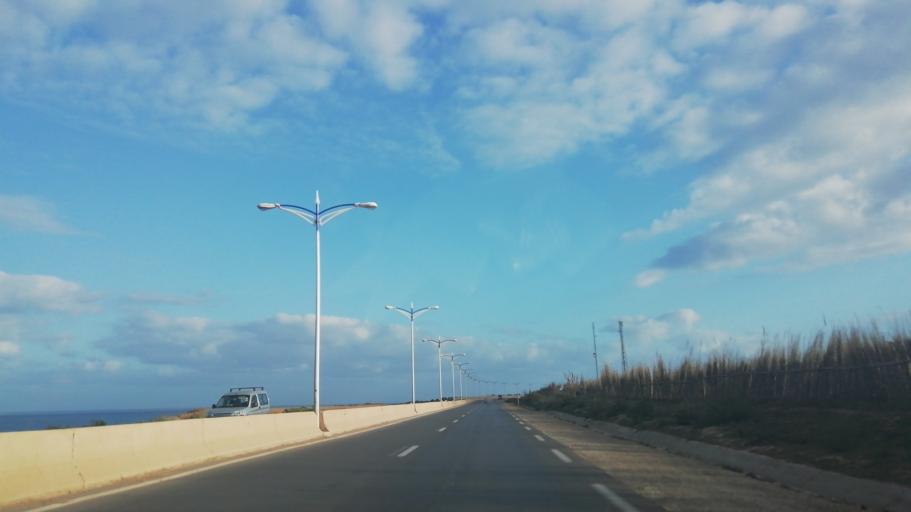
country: DZ
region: Mostaganem
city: Mostaganem
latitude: 36.0438
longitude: 0.1456
